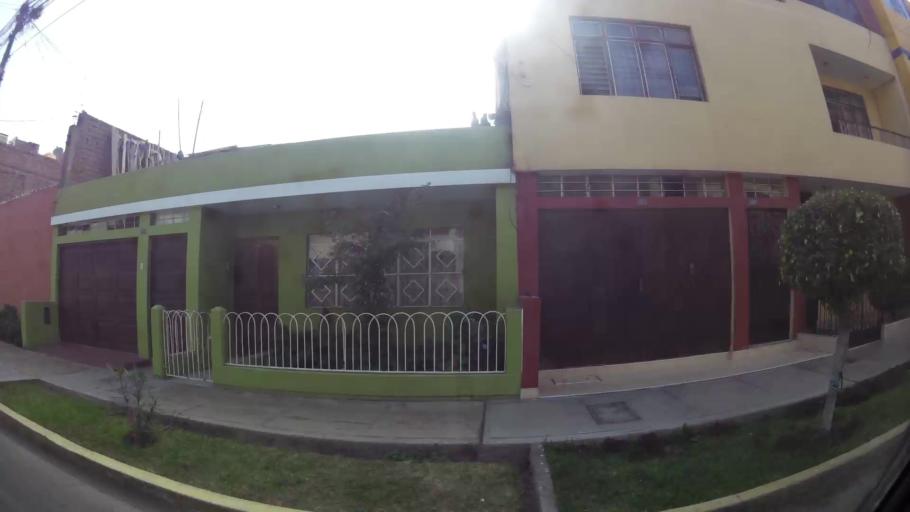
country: PE
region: La Libertad
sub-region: Provincia de Trujillo
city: Trujillo
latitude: -8.1109
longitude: -79.0138
